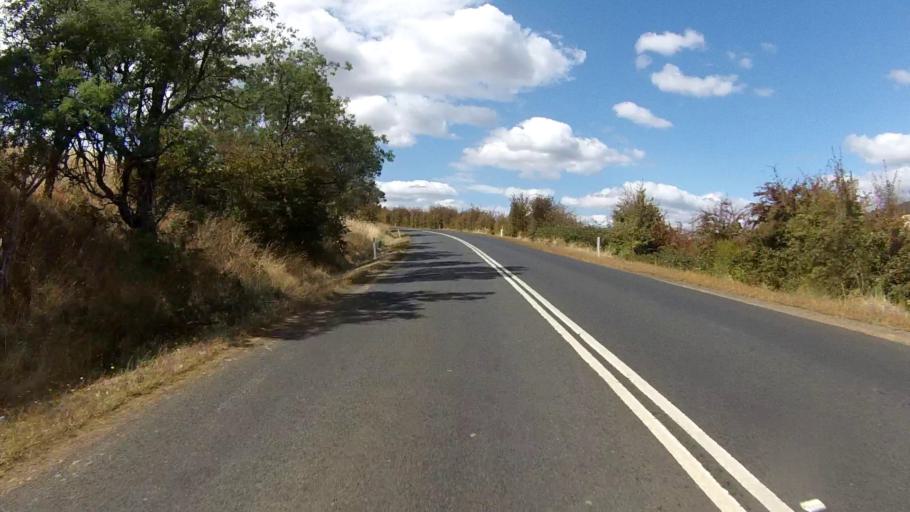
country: AU
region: Tasmania
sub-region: Derwent Valley
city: New Norfolk
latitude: -42.7367
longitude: 146.9298
